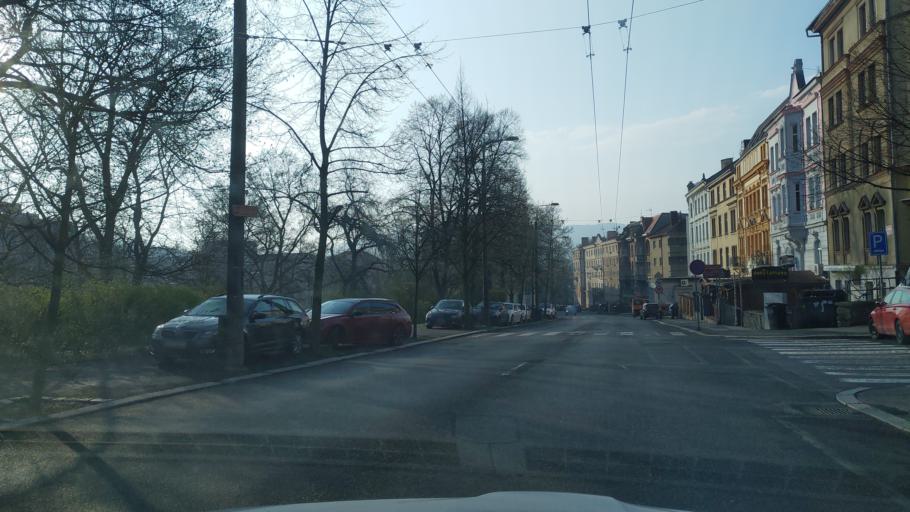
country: CZ
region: Ustecky
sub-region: Okres Usti nad Labem
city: Usti nad Labem
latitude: 50.6660
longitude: 14.0271
